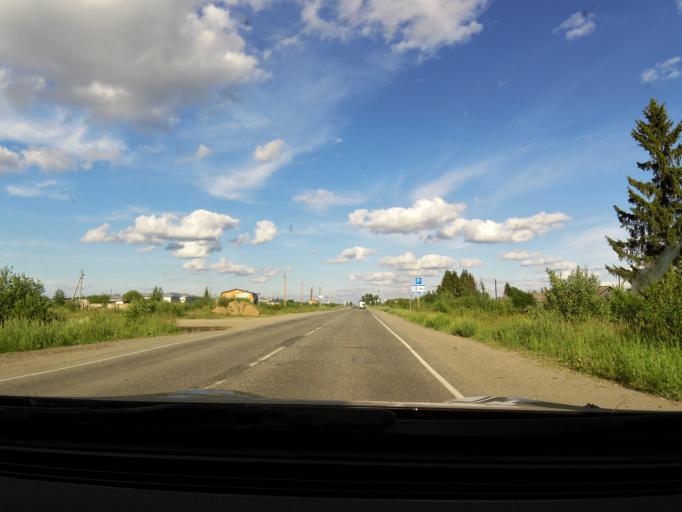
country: RU
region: Kirov
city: Omutninsk
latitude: 58.6893
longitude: 52.1782
